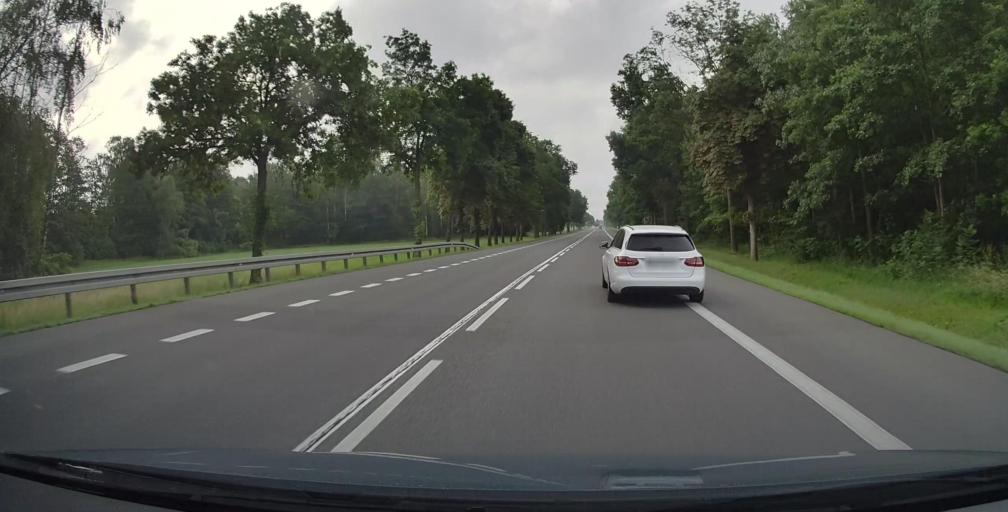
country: PL
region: Masovian Voivodeship
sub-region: Powiat siedlecki
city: Zbuczyn
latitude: 52.0811
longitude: 22.4810
